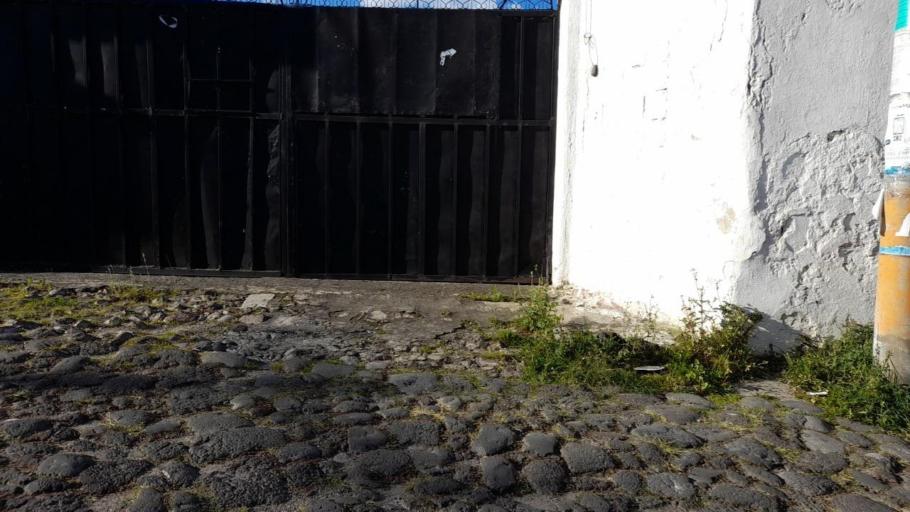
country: GT
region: Quetzaltenango
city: Quetzaltenango
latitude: 14.8370
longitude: -91.5133
